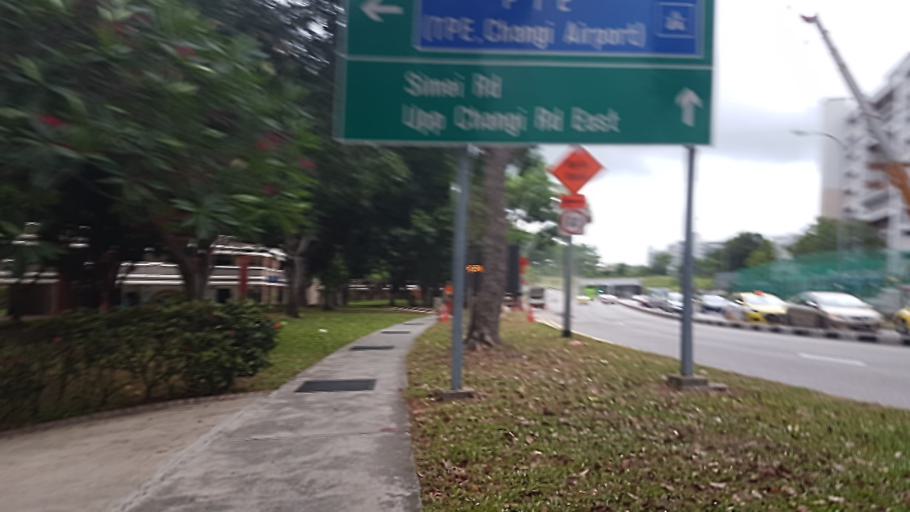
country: SG
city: Singapore
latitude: 1.3518
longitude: 103.9553
